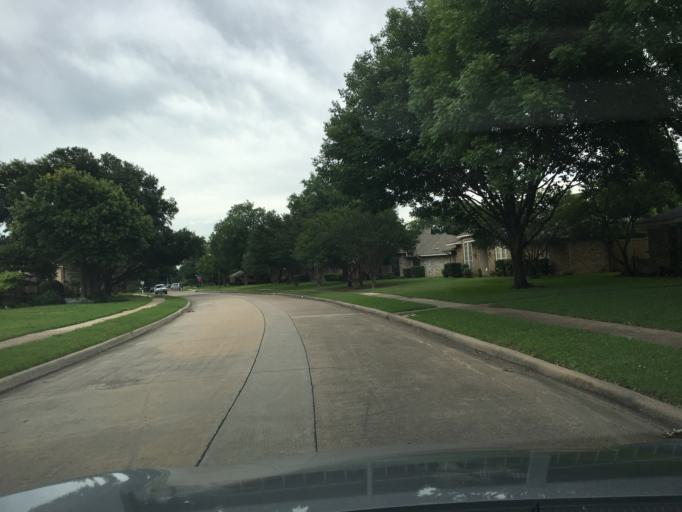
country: US
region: Texas
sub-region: Dallas County
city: Richardson
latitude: 32.9424
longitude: -96.7112
